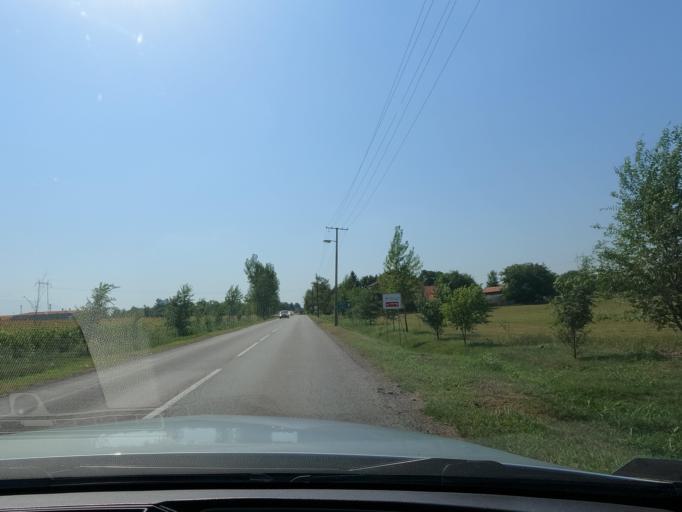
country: RS
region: Autonomna Pokrajina Vojvodina
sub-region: Severnobacki Okrug
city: Backa Topola
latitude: 45.8214
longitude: 19.6632
